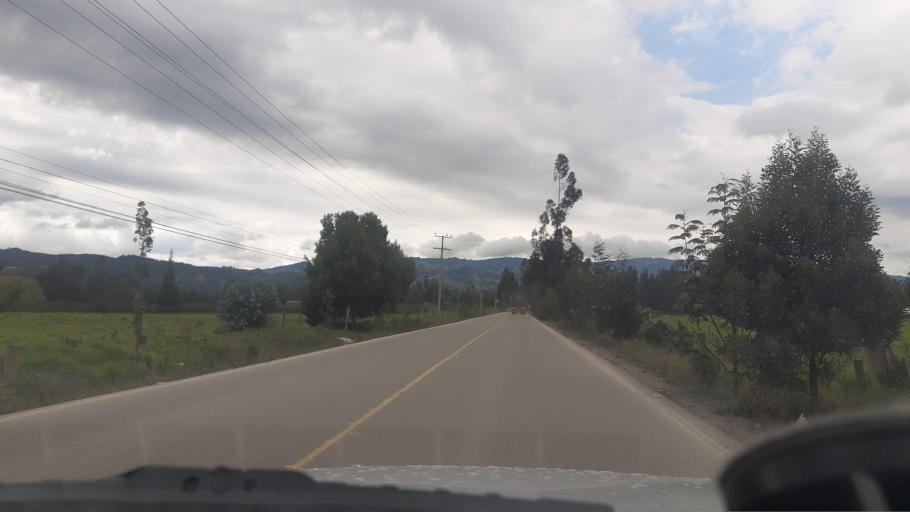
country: CO
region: Cundinamarca
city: Ubate
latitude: 5.2743
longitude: -73.7994
